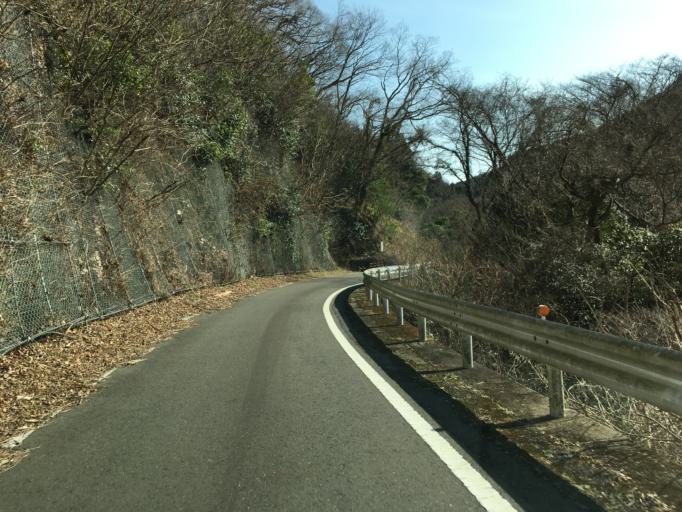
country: JP
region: Ibaraki
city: Kitaibaraki
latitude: 36.7837
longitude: 140.6765
